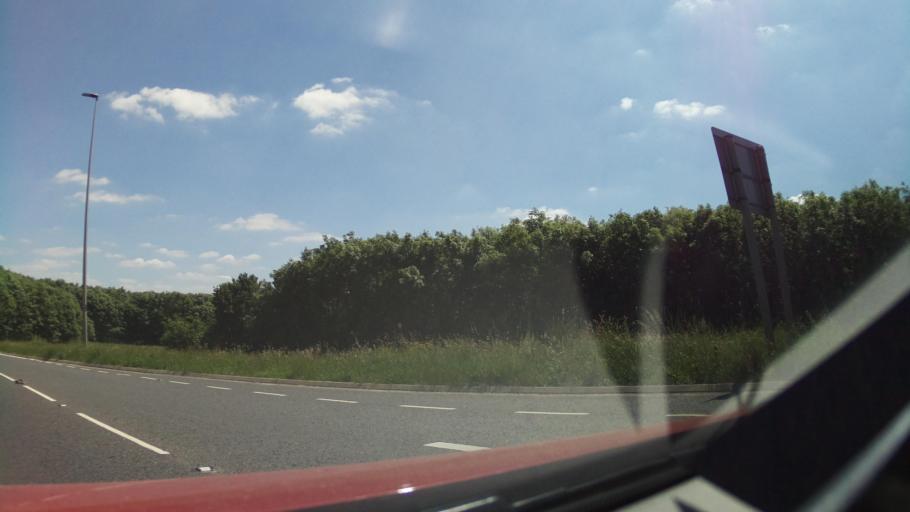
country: GB
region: England
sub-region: Wiltshire
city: Lydiard Tregoze
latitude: 51.5431
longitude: -1.8532
